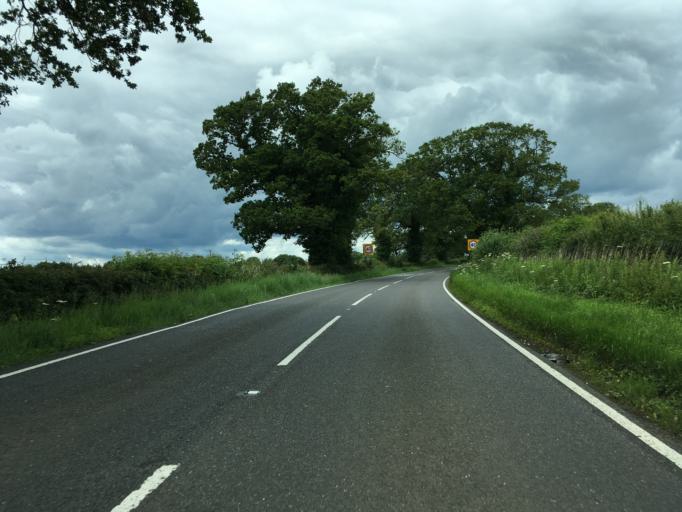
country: GB
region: England
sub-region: Northamptonshire
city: Brackley
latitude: 52.0915
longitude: -1.2345
